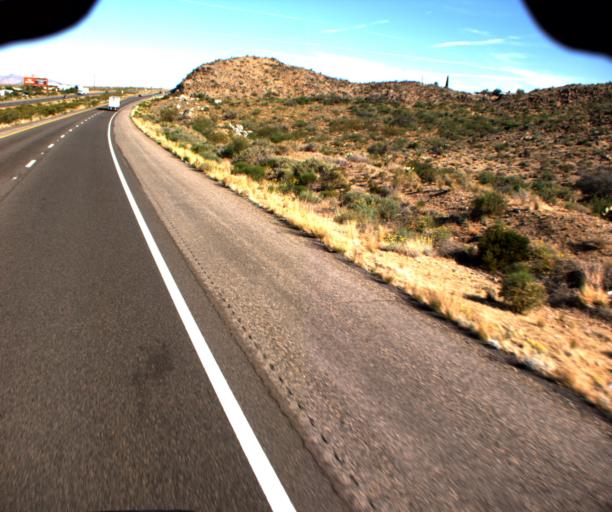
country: US
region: Arizona
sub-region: Mohave County
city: Golden Valley
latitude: 35.2395
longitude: -114.1445
